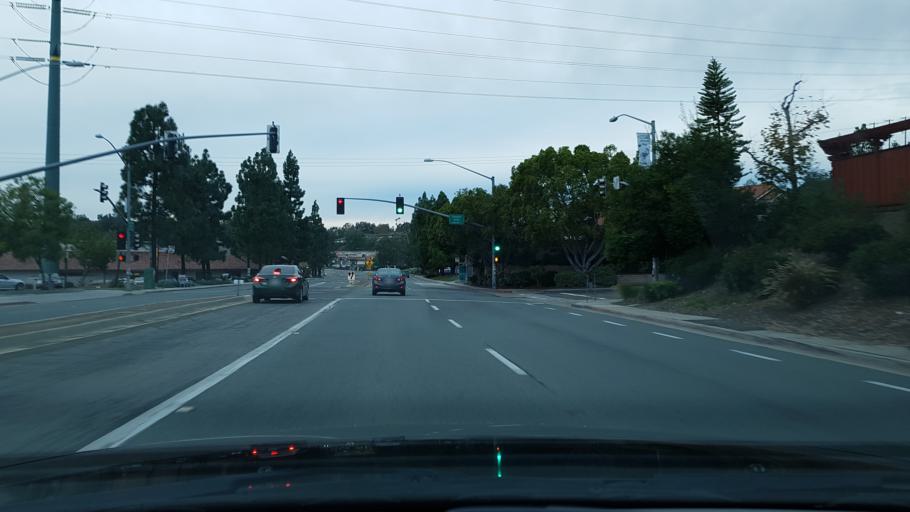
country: US
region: California
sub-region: San Diego County
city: Poway
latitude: 32.9608
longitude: -117.1102
